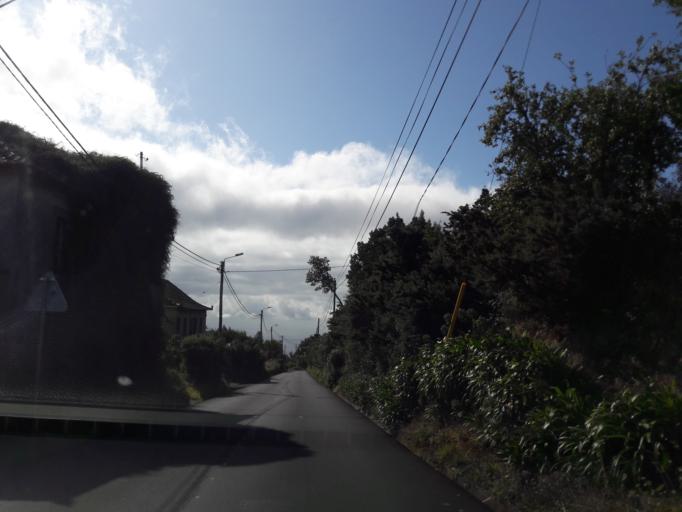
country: PT
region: Madeira
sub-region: Santa Cruz
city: Camacha
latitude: 32.6682
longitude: -16.8423
